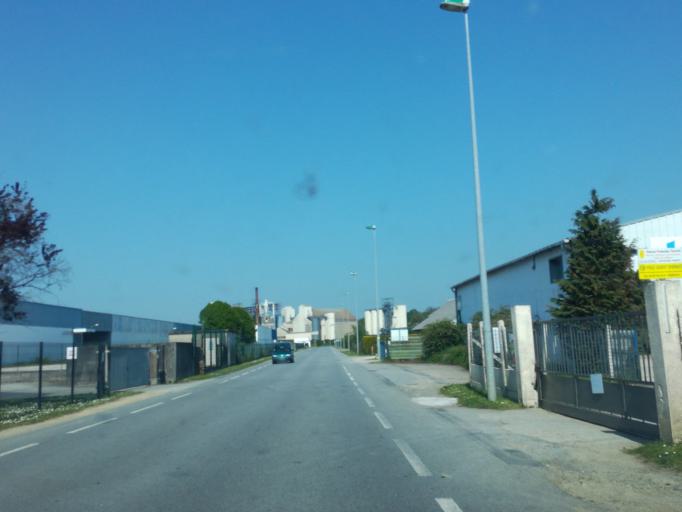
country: FR
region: Brittany
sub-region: Departement du Morbihan
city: Le Sourn
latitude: 48.0440
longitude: -2.9642
